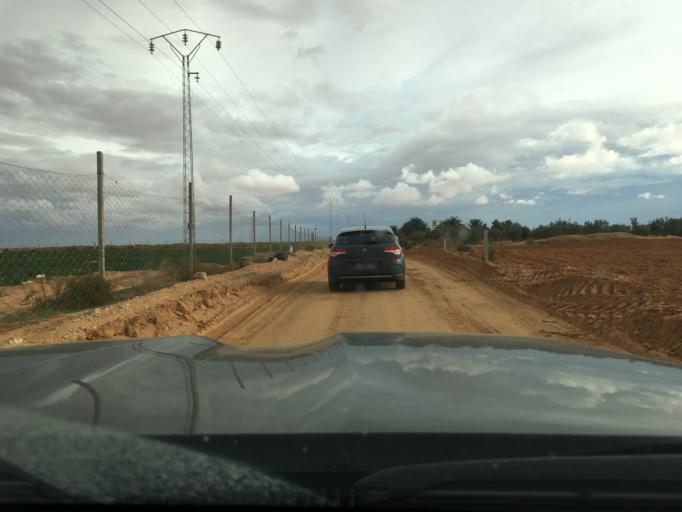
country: TN
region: Madanin
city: Medenine
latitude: 33.2764
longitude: 10.5606
